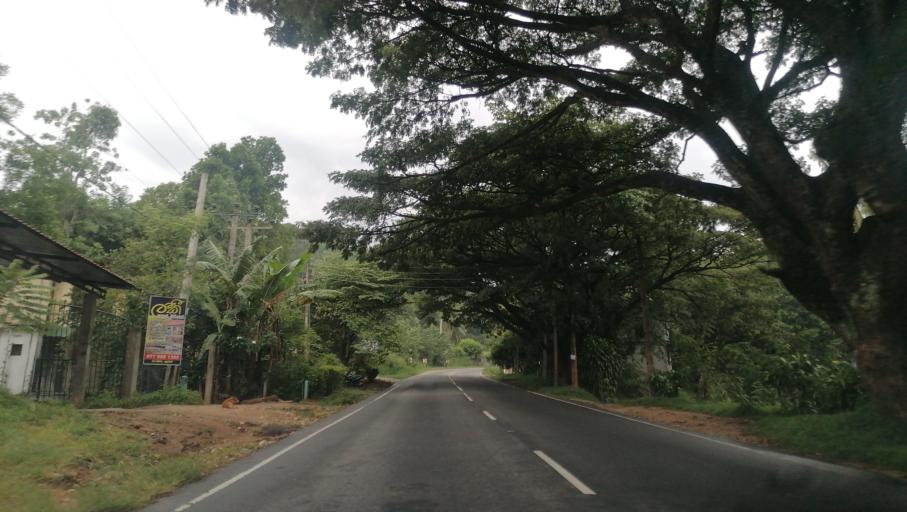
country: LK
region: Central
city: Kandy
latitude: 7.2531
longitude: 80.7300
